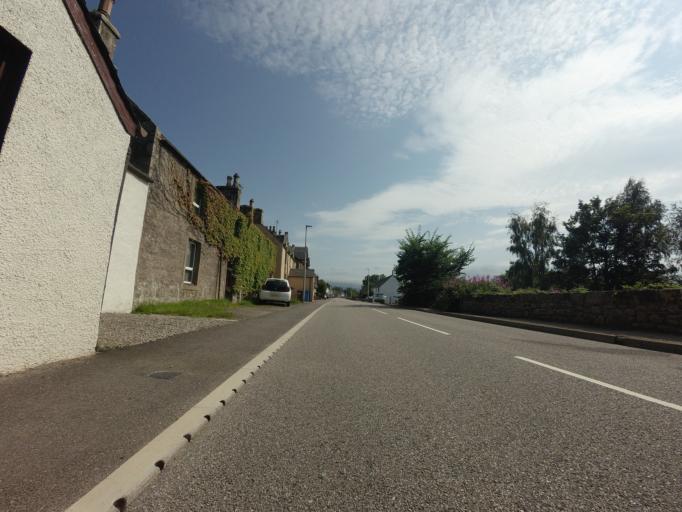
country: GB
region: Scotland
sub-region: Highland
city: Alness
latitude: 57.8953
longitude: -4.3483
